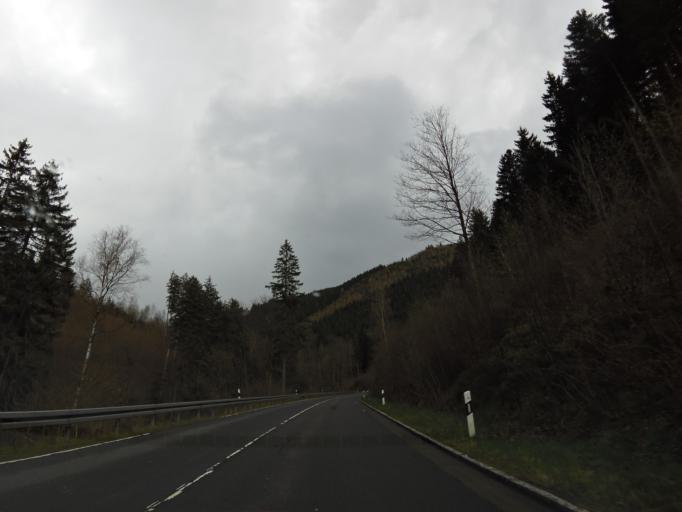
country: DE
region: Lower Saxony
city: Schulenberg im Oberharz
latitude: 51.8616
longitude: 10.4726
